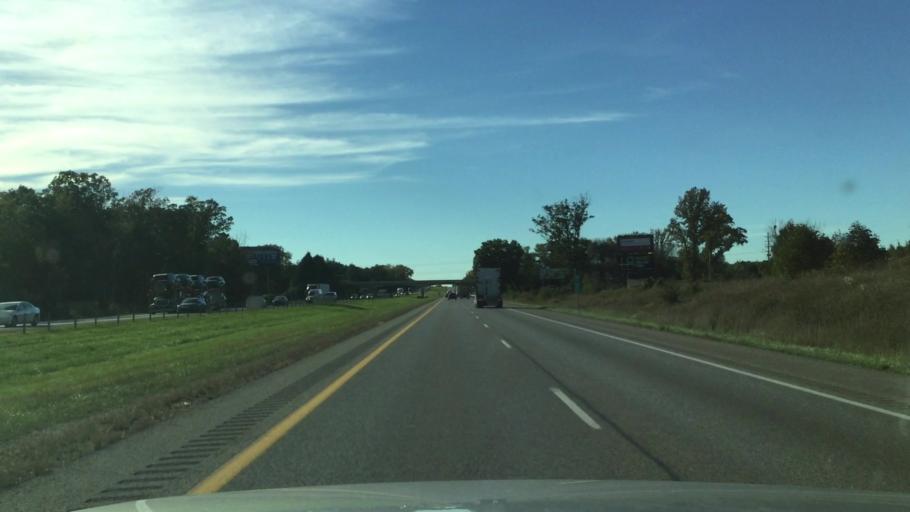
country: US
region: Michigan
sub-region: Calhoun County
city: Springfield
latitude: 42.2686
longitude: -85.2737
